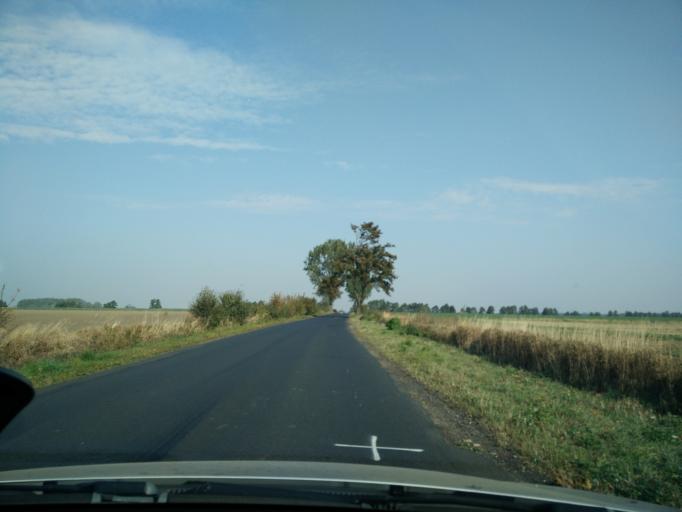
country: PL
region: Greater Poland Voivodeship
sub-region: Powiat sredzki
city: Dominowo
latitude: 52.2729
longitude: 17.3171
